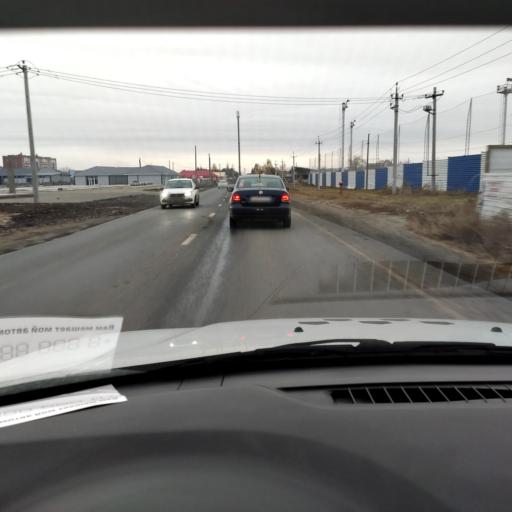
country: RU
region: Samara
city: Tol'yatti
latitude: 53.5119
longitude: 49.2450
